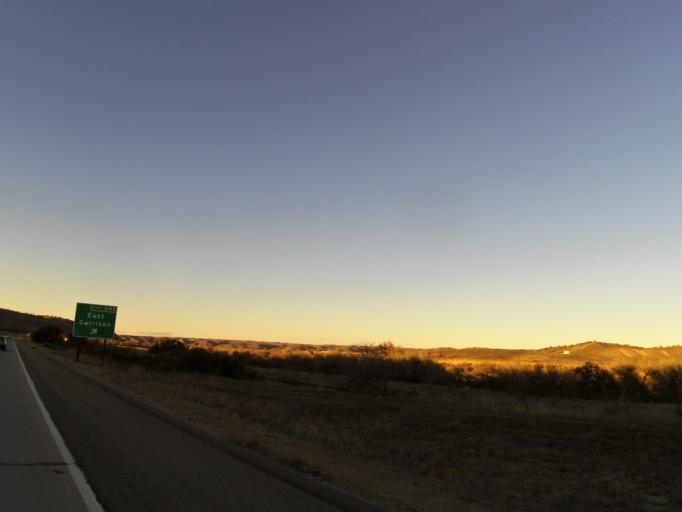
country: US
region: California
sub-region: San Luis Obispo County
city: San Miguel
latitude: 35.8090
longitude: -120.7508
